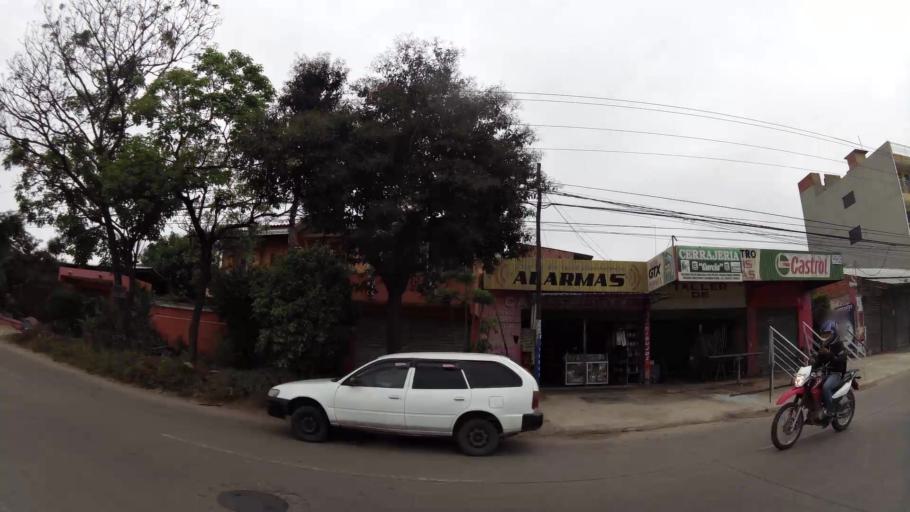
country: BO
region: Santa Cruz
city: Santa Cruz de la Sierra
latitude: -17.8213
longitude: -63.1741
